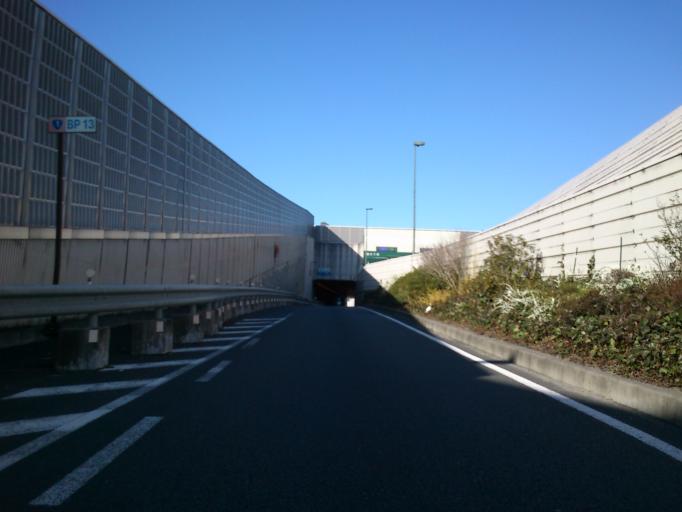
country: JP
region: Kyoto
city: Tanabe
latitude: 34.8171
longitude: 135.7186
